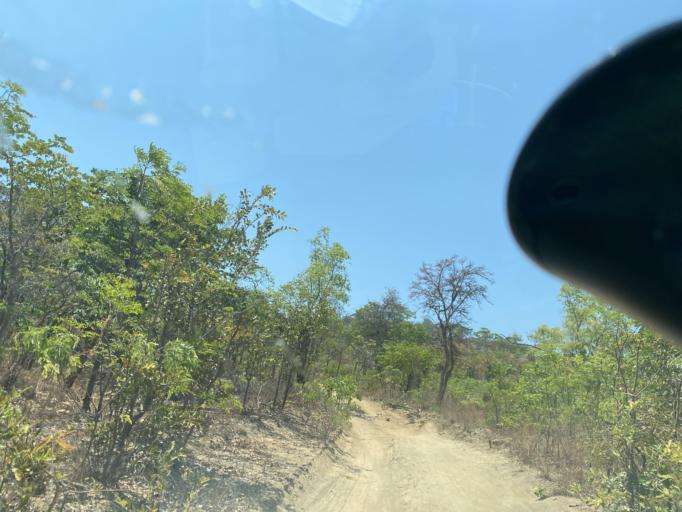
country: ZM
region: Lusaka
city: Chongwe
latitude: -15.4410
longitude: 29.2045
